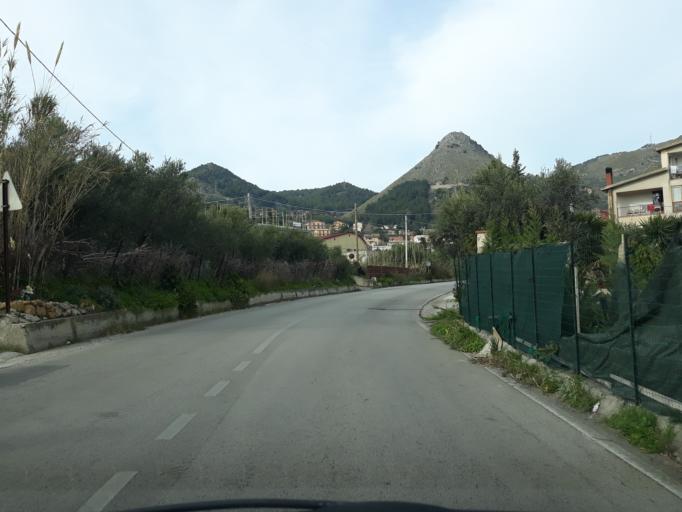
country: IT
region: Sicily
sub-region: Palermo
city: Giardinello
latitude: 38.0843
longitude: 13.1633
